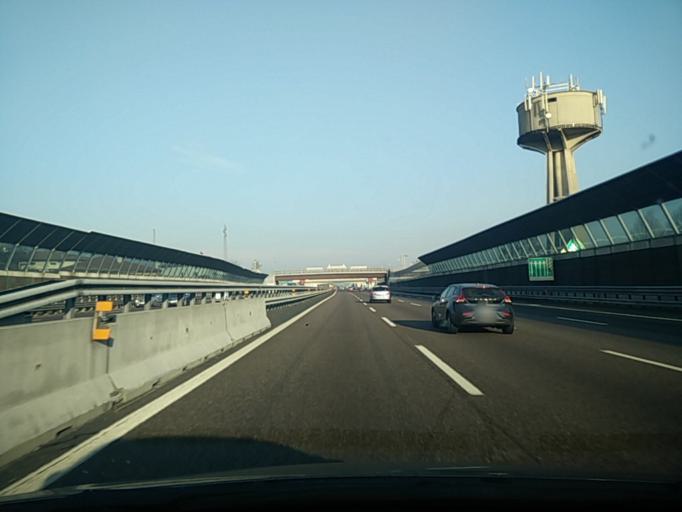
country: IT
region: Lombardy
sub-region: Provincia di Bergamo
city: Osio Sopra
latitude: 45.6292
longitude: 9.5941
